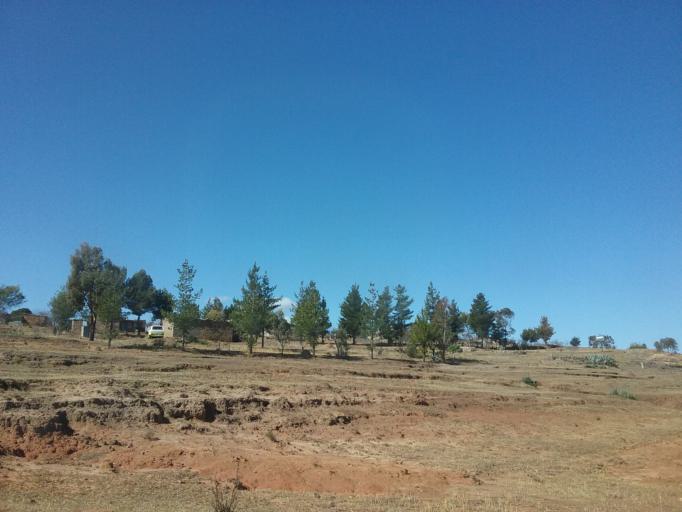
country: LS
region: Maseru
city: Maseru
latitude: -29.4675
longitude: 27.5782
